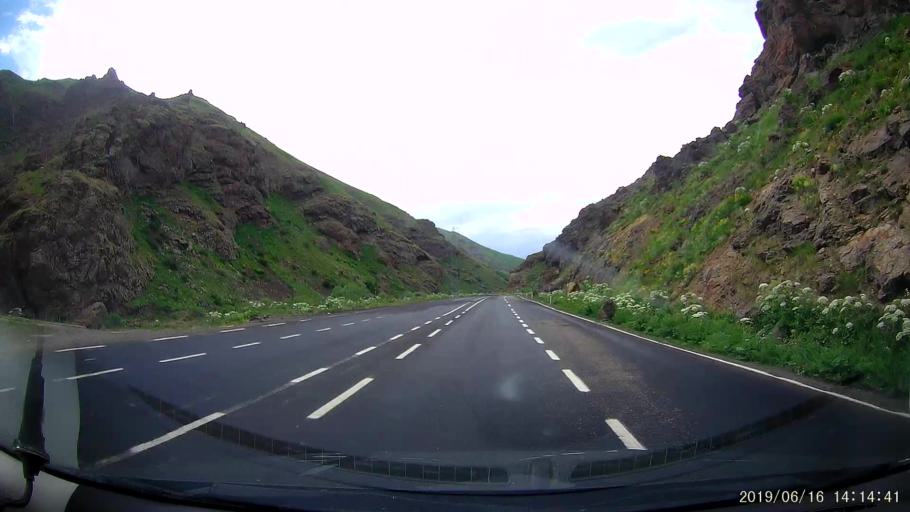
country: TR
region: Agri
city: Tahir
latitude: 39.7970
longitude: 42.4922
